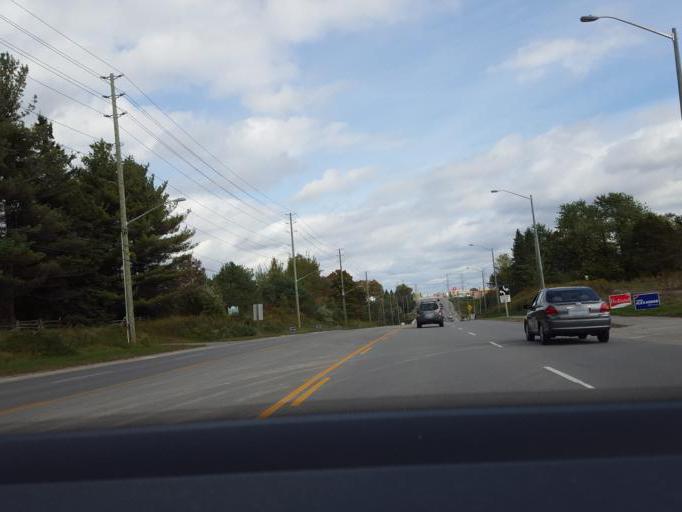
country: CA
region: Ontario
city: Ajax
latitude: 43.8904
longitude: -79.0637
